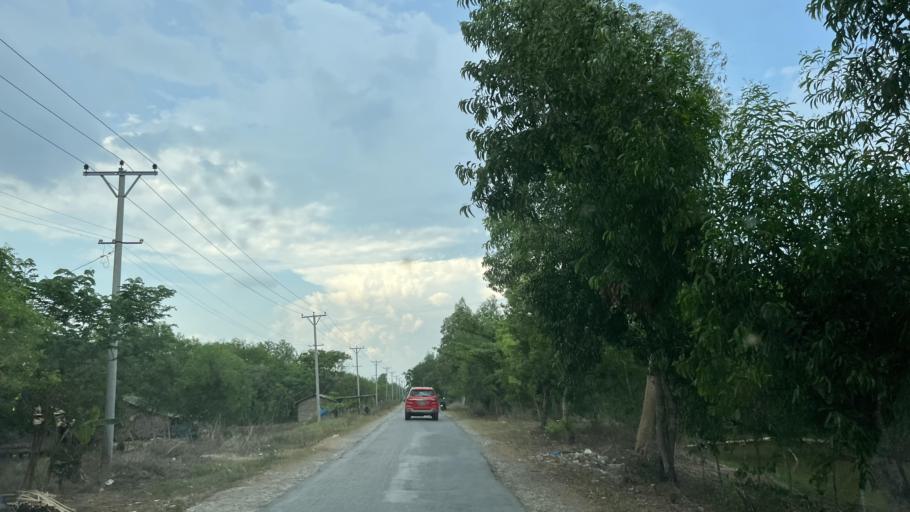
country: MM
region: Ayeyarwady
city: Pyapon
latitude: 16.1229
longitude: 95.6578
